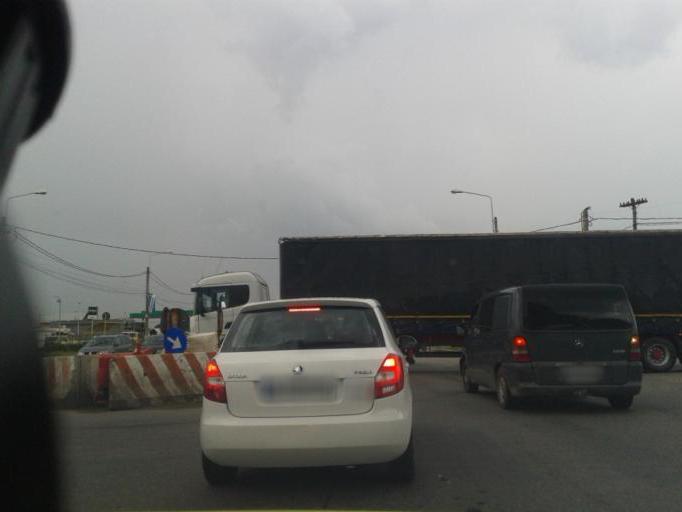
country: RO
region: Prahova
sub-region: Comuna Bucov
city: Bucov
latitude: 44.9564
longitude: 26.0505
